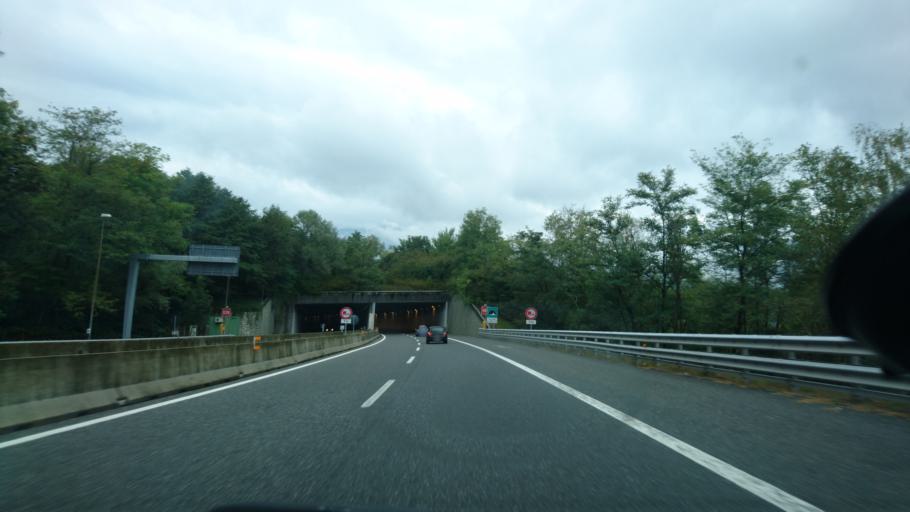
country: IT
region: Piedmont
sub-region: Provincia Verbano-Cusio-Ossola
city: Baveno
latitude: 45.9206
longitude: 8.4852
